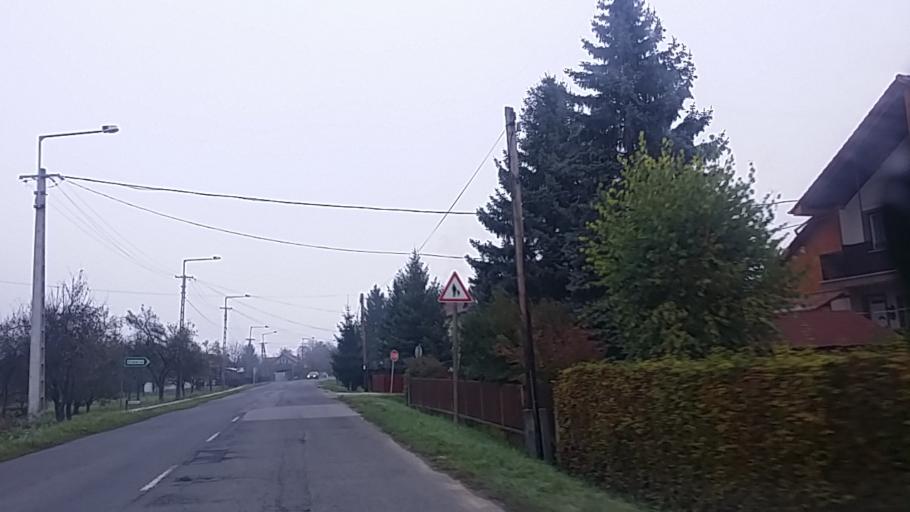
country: HU
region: Borsod-Abauj-Zemplen
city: Sajokaza
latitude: 48.2430
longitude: 20.5220
